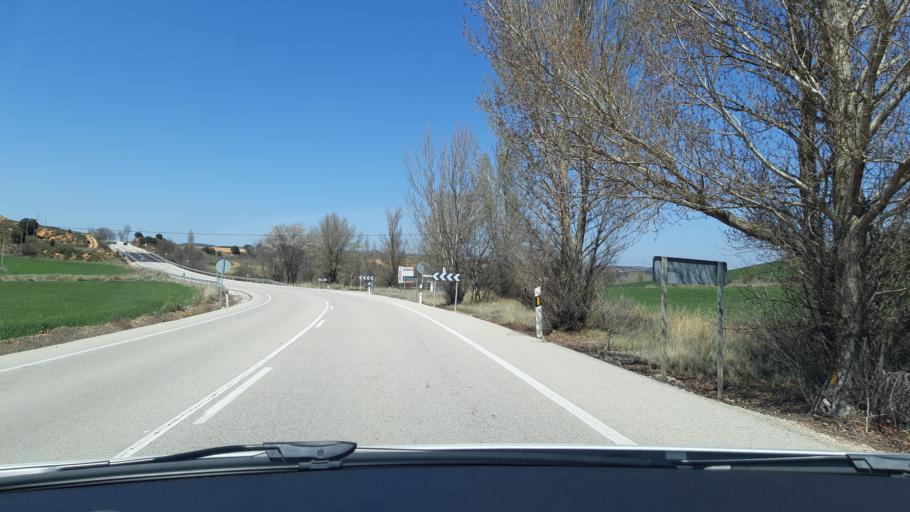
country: ES
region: Castille-La Mancha
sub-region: Provincia de Guadalajara
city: Masegoso de Tajuna
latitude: 40.8065
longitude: -2.6714
